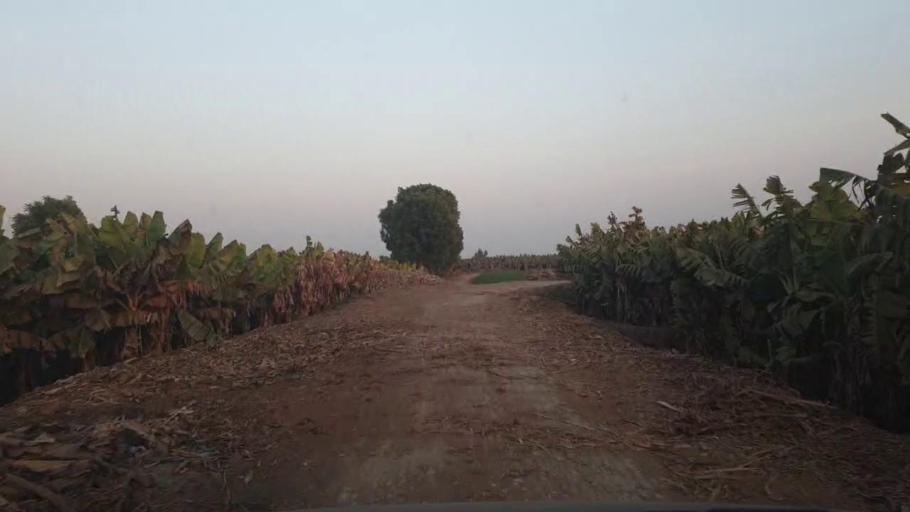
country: PK
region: Sindh
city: Bhit Shah
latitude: 25.8474
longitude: 68.5200
